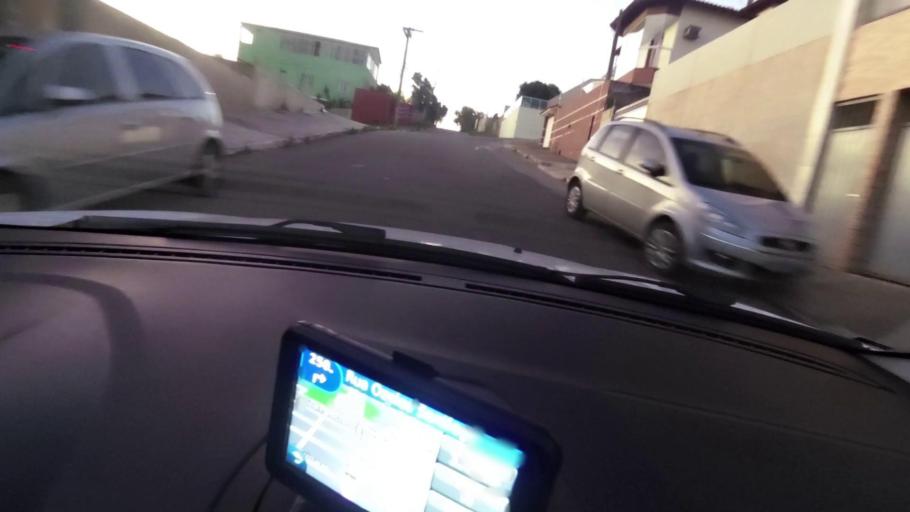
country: BR
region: Espirito Santo
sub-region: Guarapari
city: Guarapari
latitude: -20.6635
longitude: -40.5075
